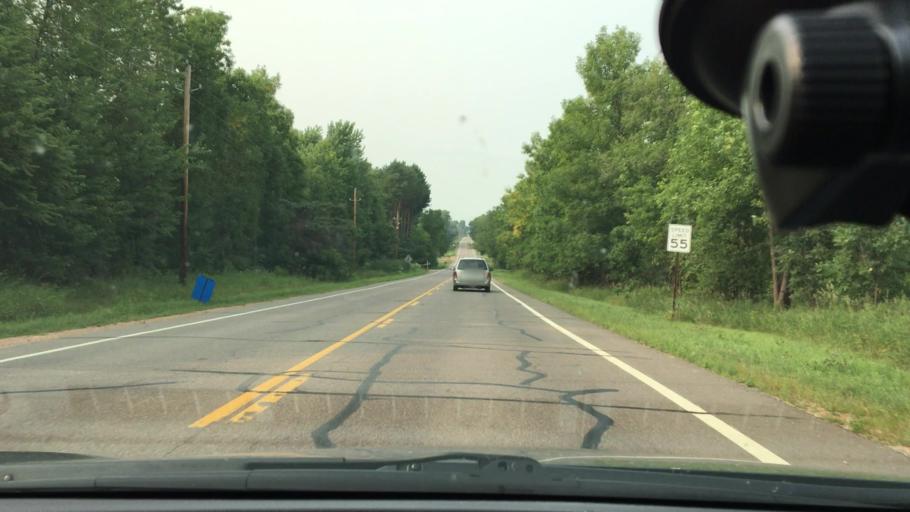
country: US
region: Minnesota
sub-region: Hennepin County
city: Champlin
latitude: 45.1669
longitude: -93.4621
